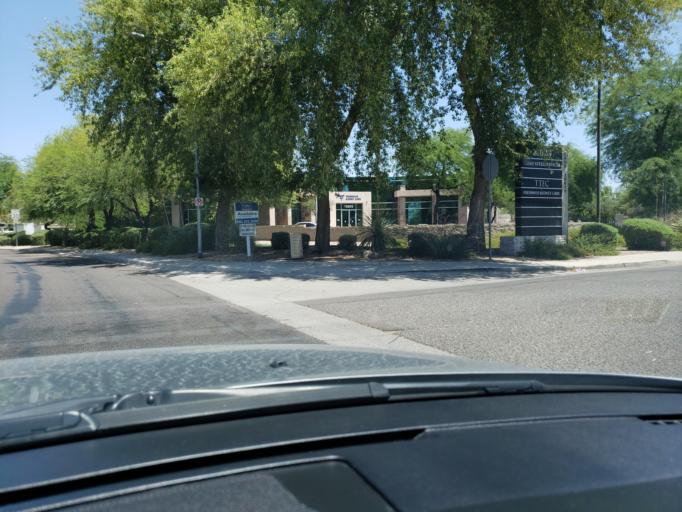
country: US
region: Arizona
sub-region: Maricopa County
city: Glendale
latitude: 33.6361
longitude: -112.1187
